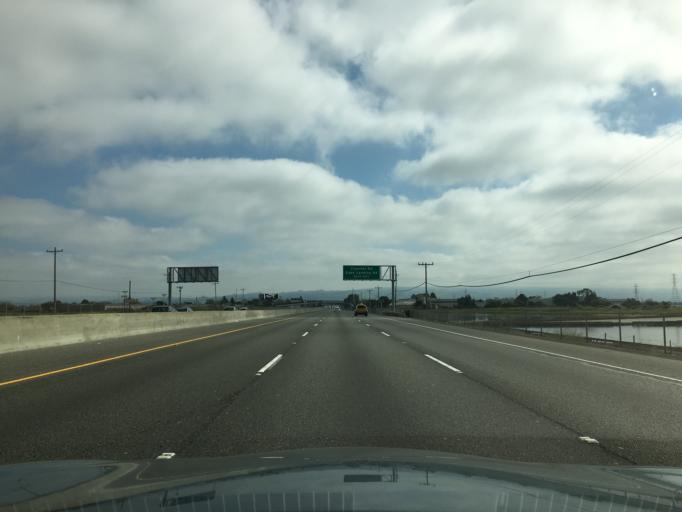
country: US
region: California
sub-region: Alameda County
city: San Lorenzo
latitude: 37.6232
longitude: -122.1358
